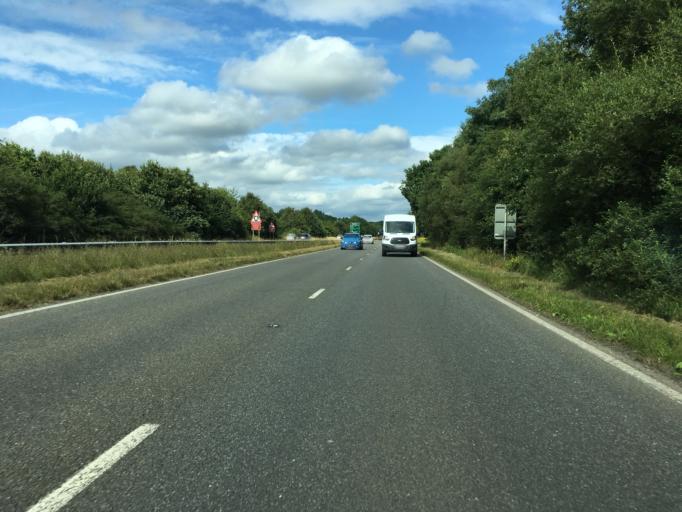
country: GB
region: England
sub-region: West Sussex
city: Horsham
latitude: 51.0754
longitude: -0.3438
